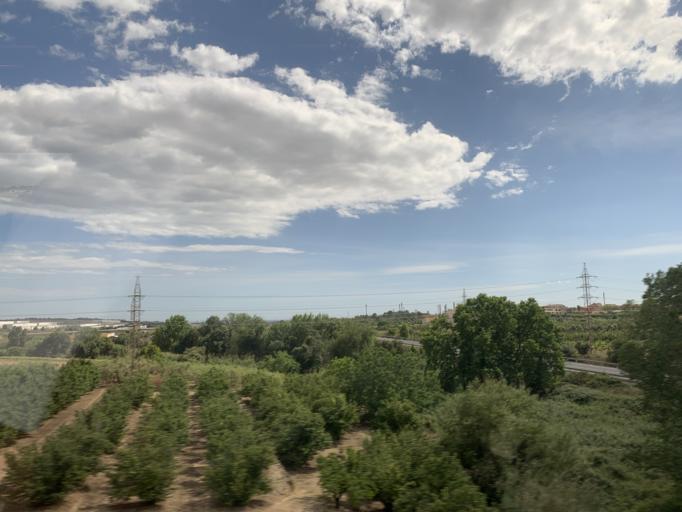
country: ES
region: Catalonia
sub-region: Provincia de Tarragona
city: la Pobla de Mafumet
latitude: 41.1980
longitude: 1.2439
